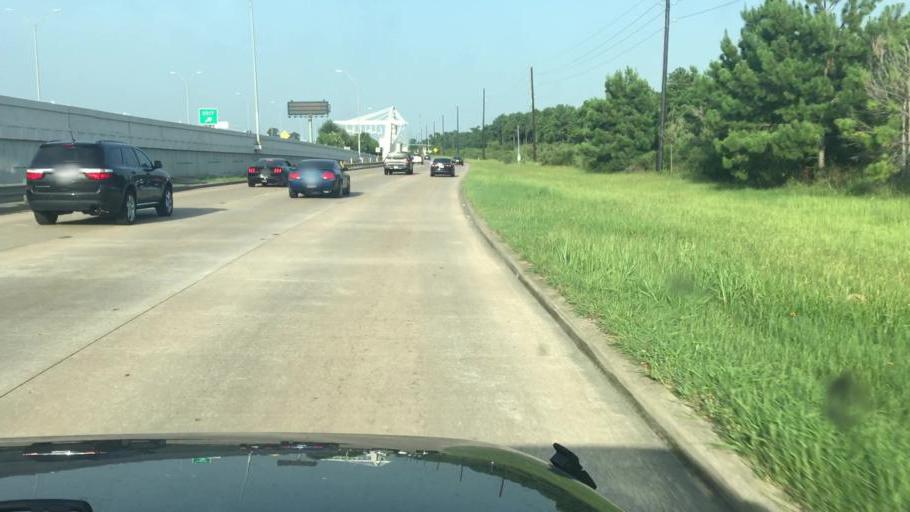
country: US
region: Texas
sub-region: Harris County
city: Humble
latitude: 29.9337
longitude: -95.2313
